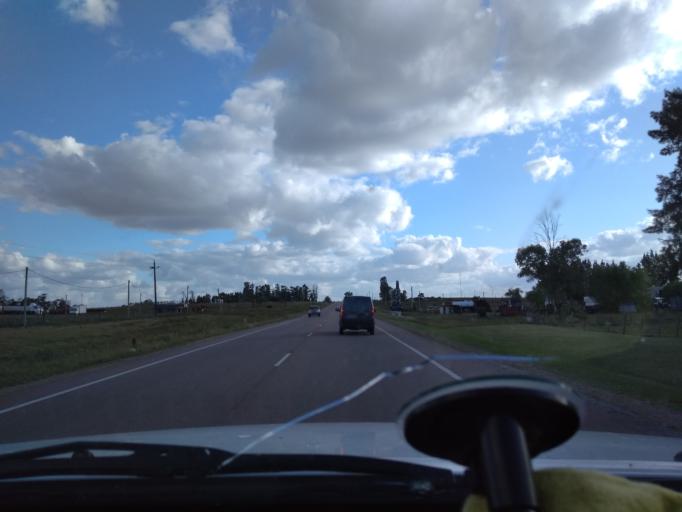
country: UY
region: Canelones
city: Tala
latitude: -34.4366
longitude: -55.8220
